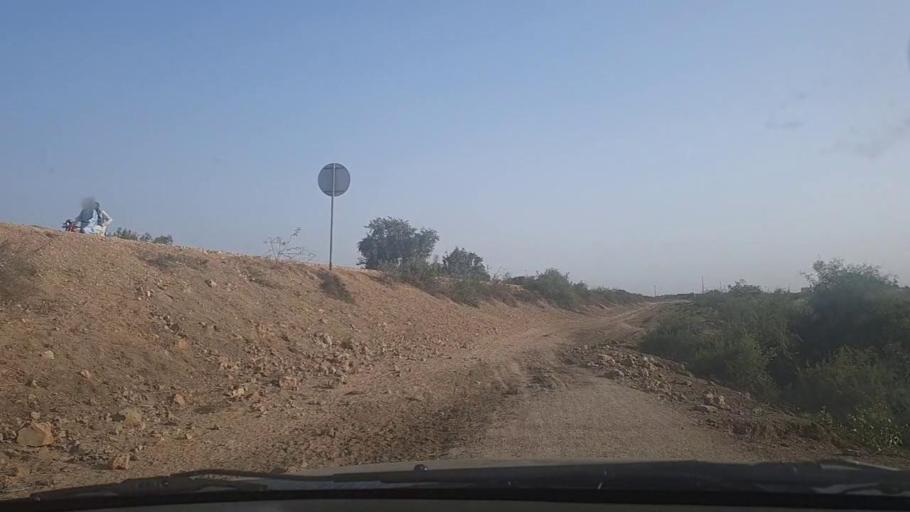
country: PK
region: Sindh
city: Keti Bandar
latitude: 24.2891
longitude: 67.6158
